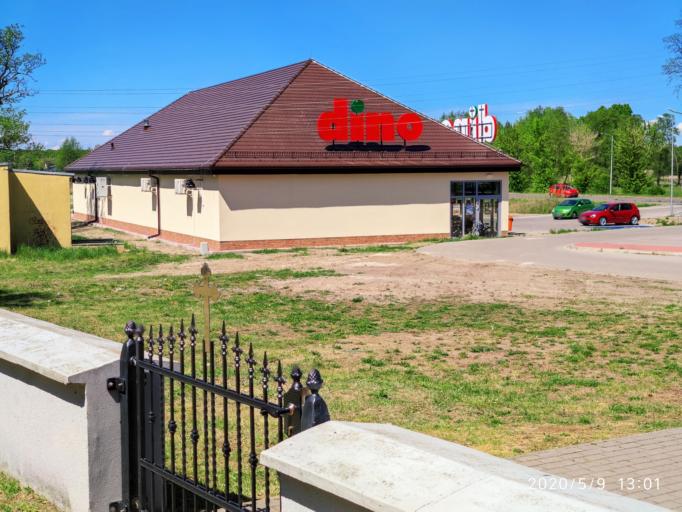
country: PL
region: Lubusz
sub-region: Powiat zielonogorski
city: Babimost
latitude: 52.1628
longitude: 15.8255
